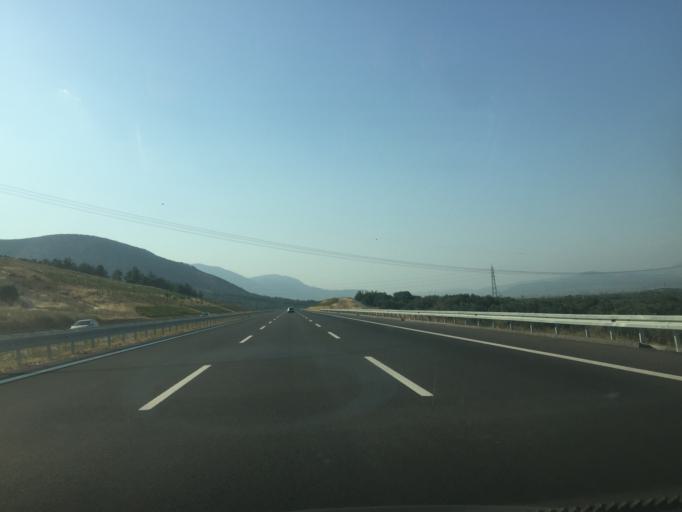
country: TR
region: Manisa
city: Kirkagac
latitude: 39.0581
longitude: 27.7262
